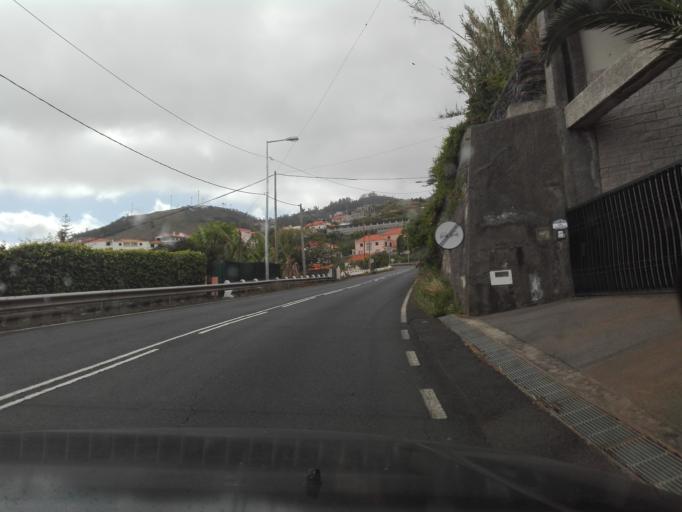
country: PT
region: Madeira
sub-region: Santa Cruz
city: Santa Cruz
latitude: 32.6592
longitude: -16.8181
